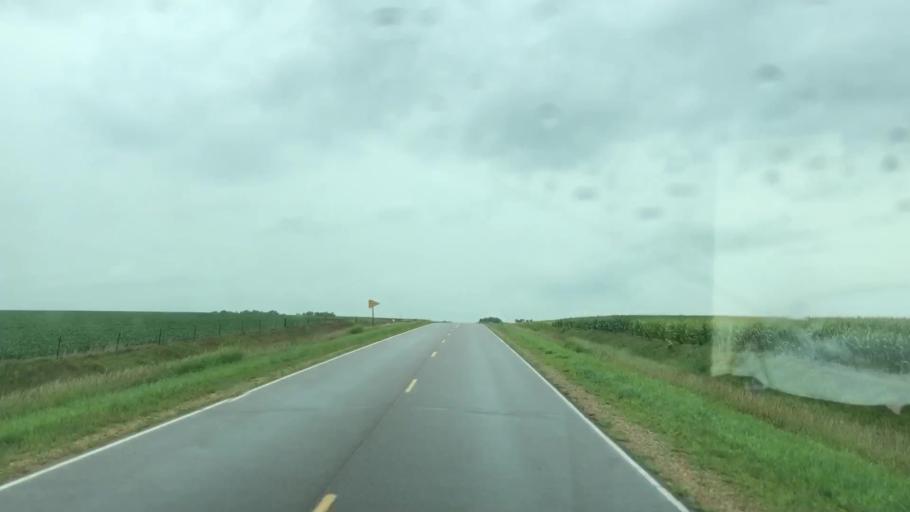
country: US
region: Iowa
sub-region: O'Brien County
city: Sanborn
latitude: 43.2301
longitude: -95.7234
